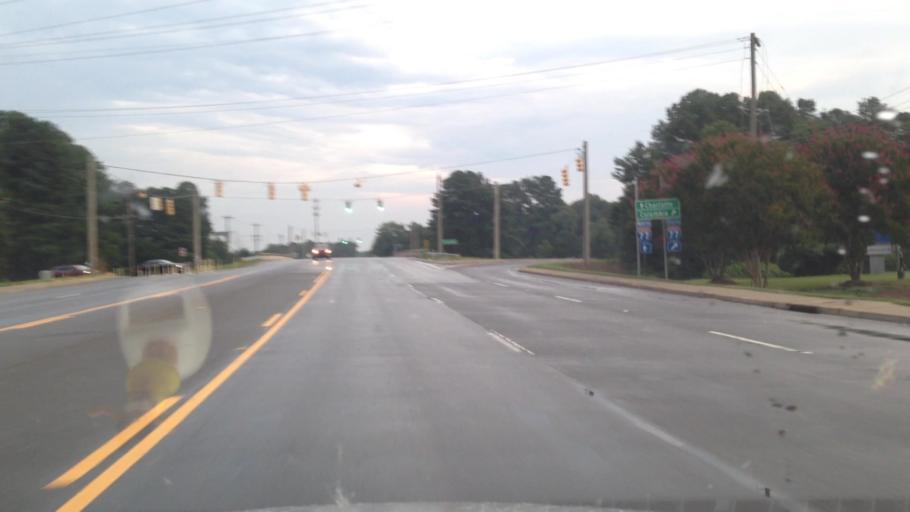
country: US
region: South Carolina
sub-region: York County
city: Fort Mill
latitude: 35.0610
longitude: -80.9580
